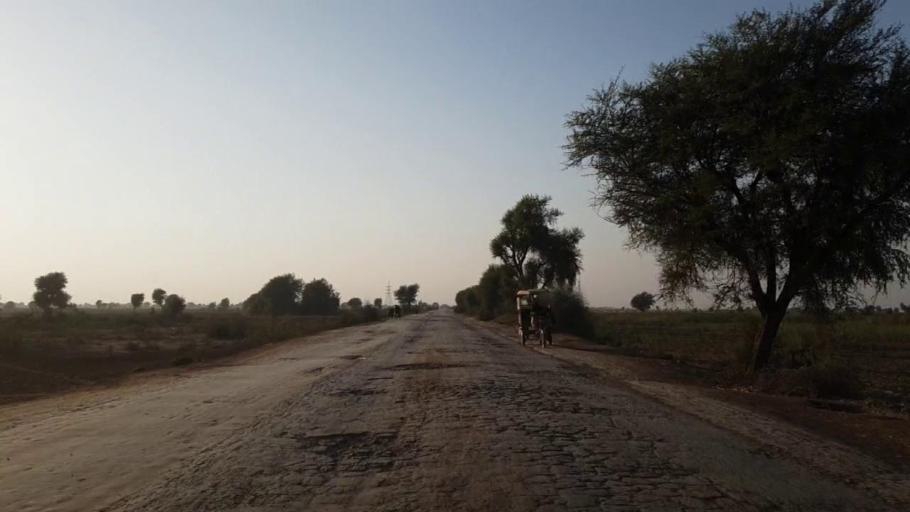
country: PK
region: Sindh
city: Chambar
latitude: 25.2133
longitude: 68.7748
